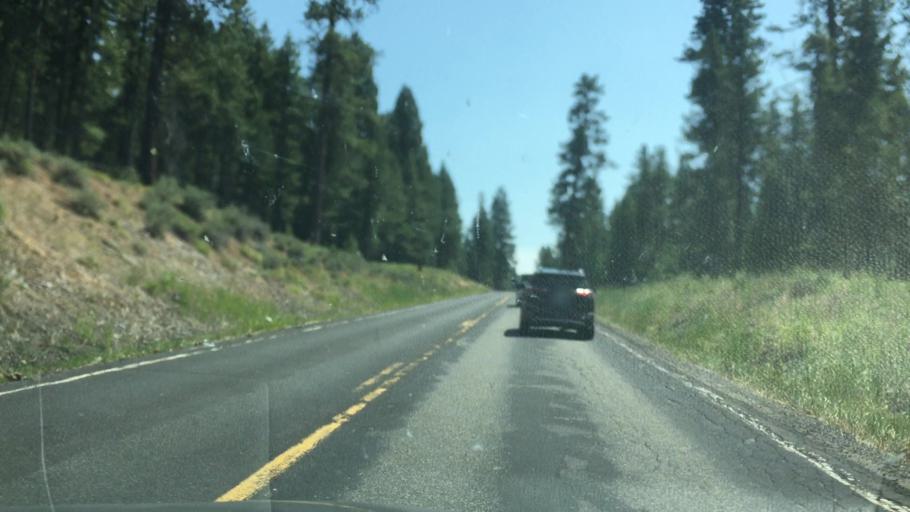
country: US
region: Idaho
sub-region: Valley County
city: McCall
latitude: 44.9433
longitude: -116.1673
